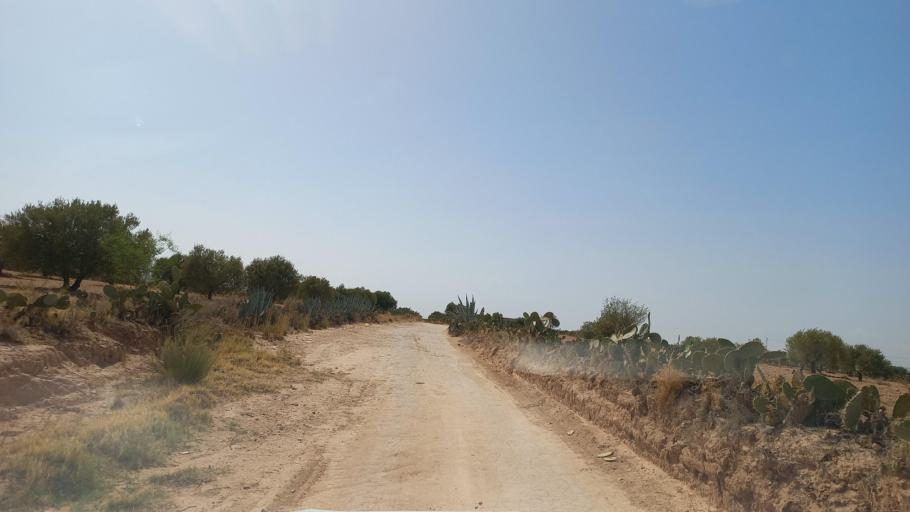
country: TN
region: Al Qasrayn
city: Kasserine
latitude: 35.2178
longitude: 9.0376
